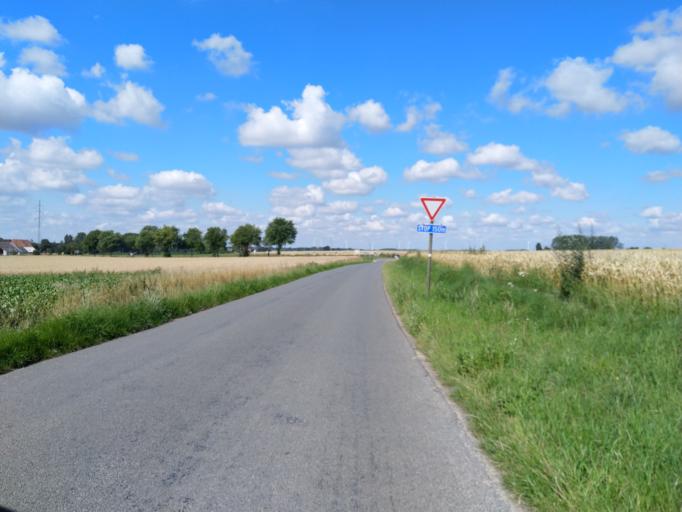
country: BE
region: Wallonia
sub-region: Province du Hainaut
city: Beloeil
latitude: 50.5932
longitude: 3.7305
